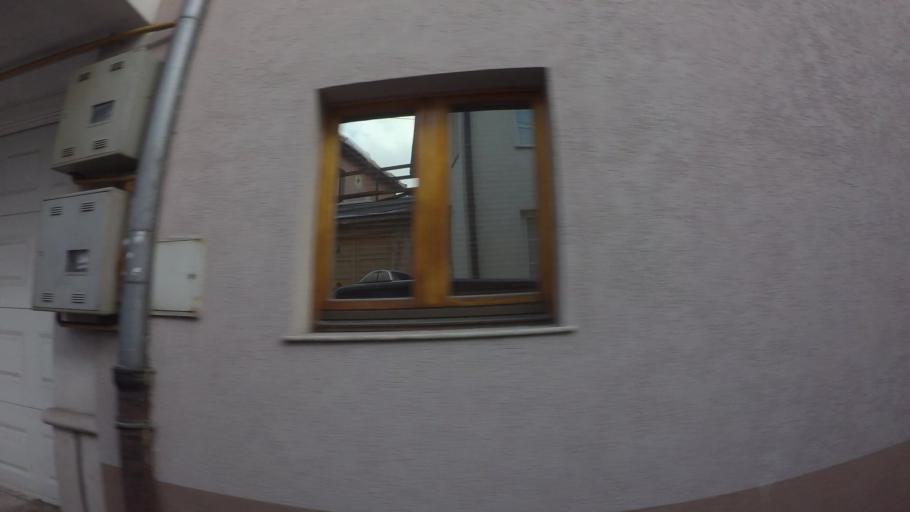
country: BA
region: Federation of Bosnia and Herzegovina
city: Kobilja Glava
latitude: 43.8629
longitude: 18.4307
